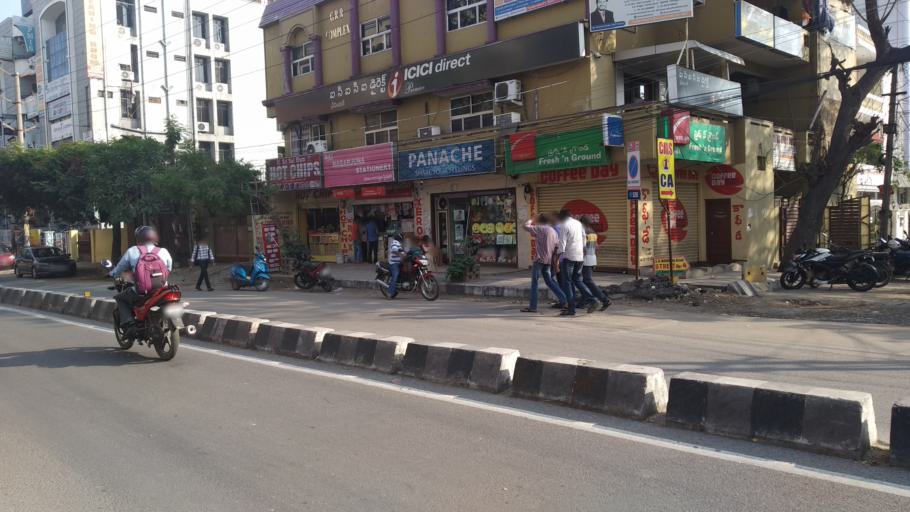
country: IN
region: Telangana
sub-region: Rangareddi
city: Kukatpalli
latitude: 17.4422
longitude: 78.4442
